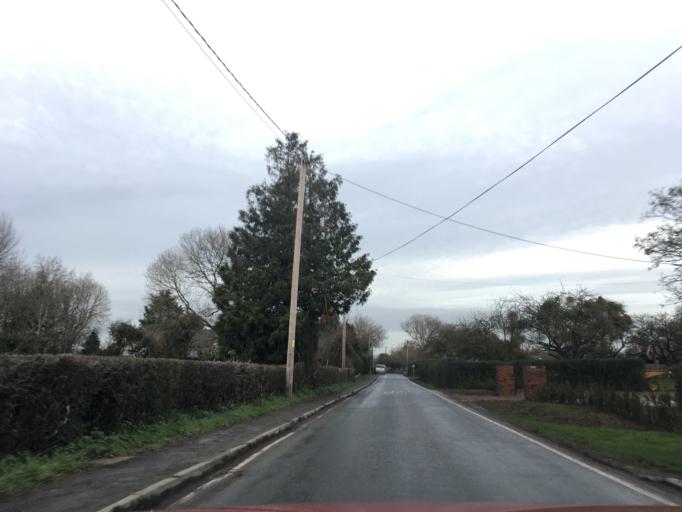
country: GB
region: Wales
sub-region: Newport
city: Redwick
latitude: 51.5533
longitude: -2.8486
